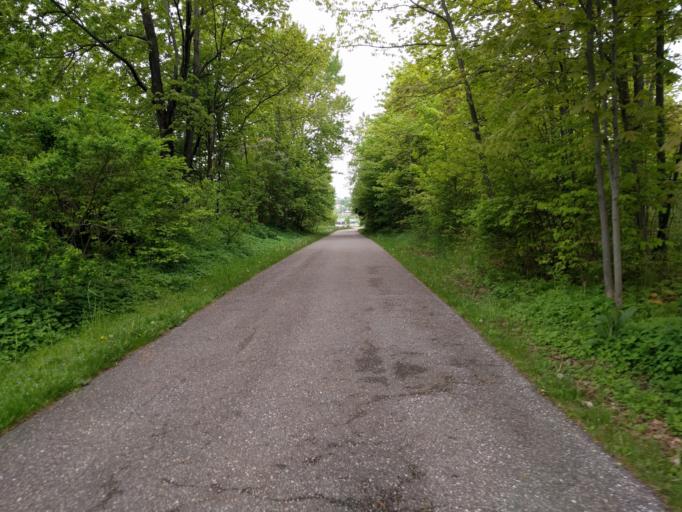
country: US
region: Michigan
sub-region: Marquette County
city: Trowbridge Park
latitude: 46.5500
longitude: -87.4180
